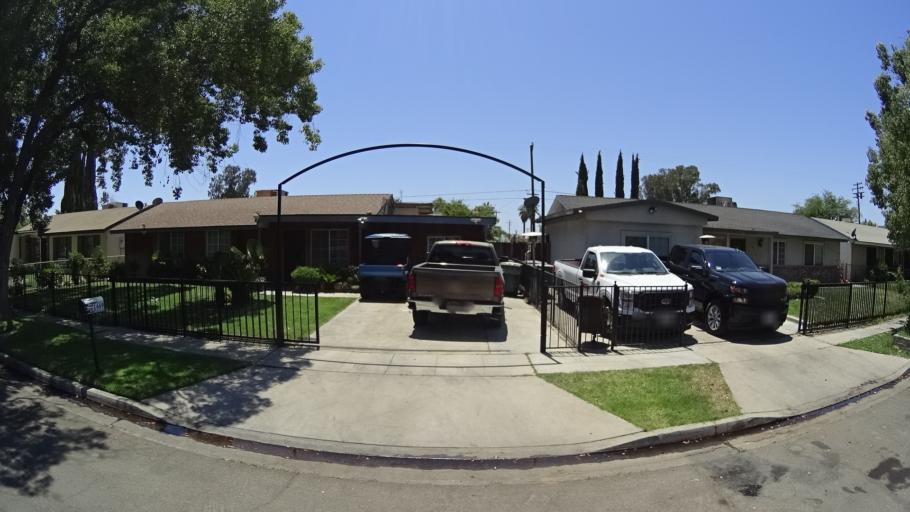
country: US
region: California
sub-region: Fresno County
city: West Park
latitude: 36.7298
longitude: -119.8309
